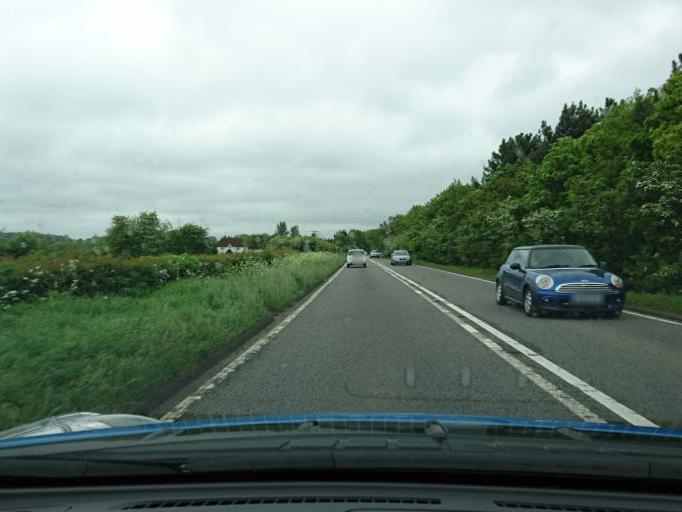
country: GB
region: England
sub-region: Oxfordshire
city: Faringdon
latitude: 51.6342
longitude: -1.6046
